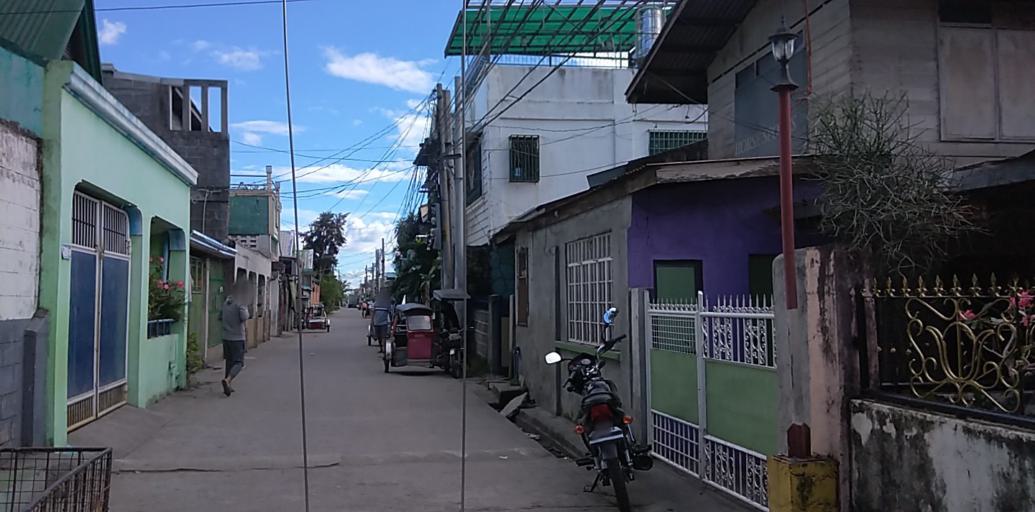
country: PH
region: Central Luzon
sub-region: Province of Pampanga
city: Arayat
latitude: 15.1429
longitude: 120.7683
